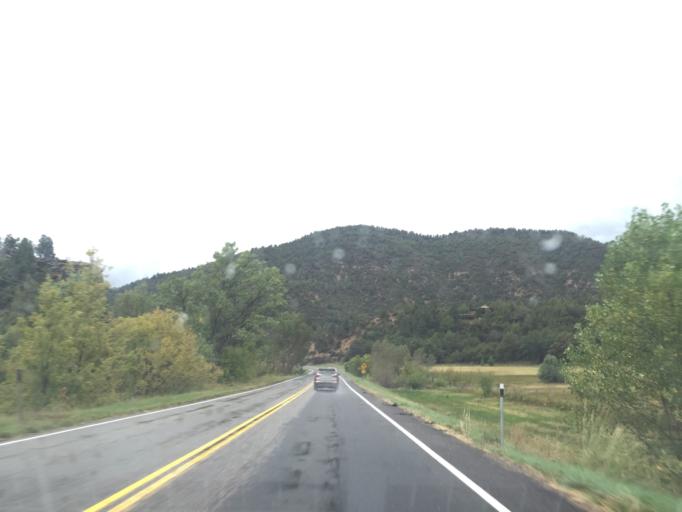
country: US
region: Utah
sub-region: Kane County
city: Kanab
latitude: 37.3438
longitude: -112.6027
